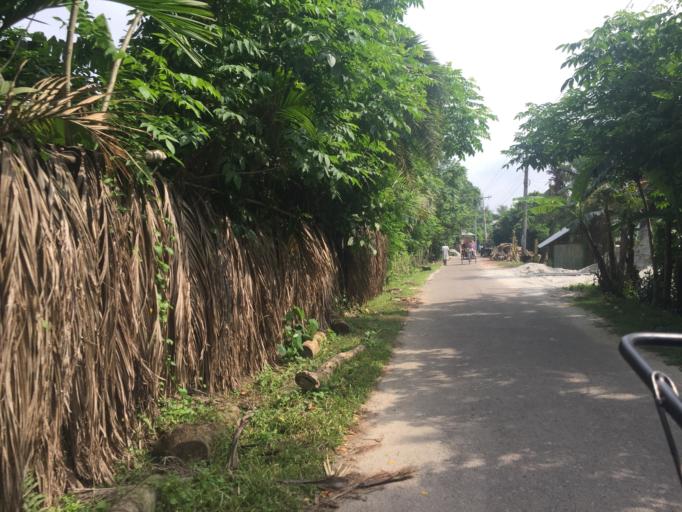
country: BD
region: Barisal
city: Mathba
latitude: 22.2429
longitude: 89.9142
